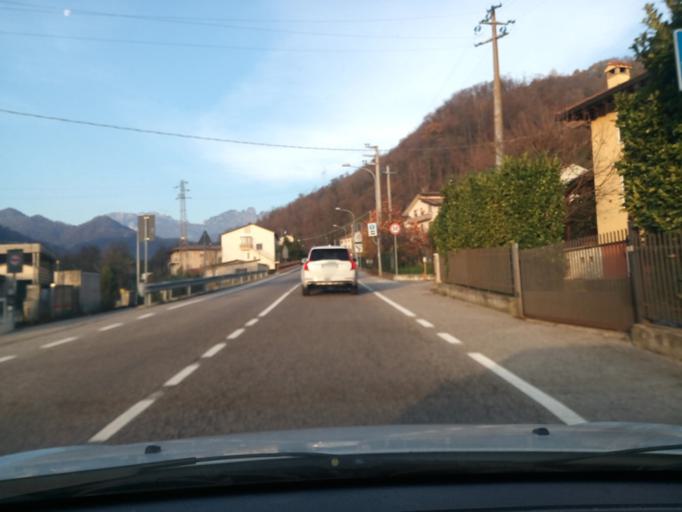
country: IT
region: Veneto
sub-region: Provincia di Vicenza
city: Torrebelvicino
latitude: 45.7187
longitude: 11.3040
